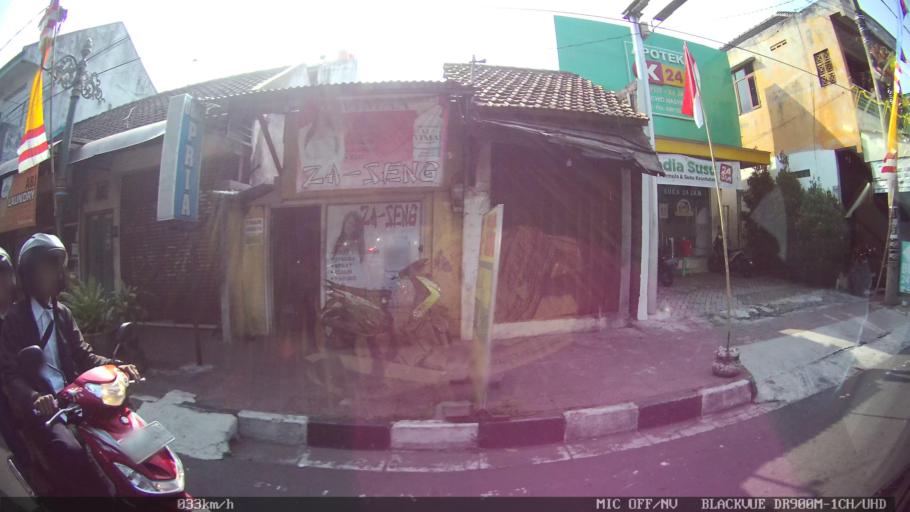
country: ID
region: Daerah Istimewa Yogyakarta
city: Yogyakarta
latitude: -7.8054
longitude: 110.3562
